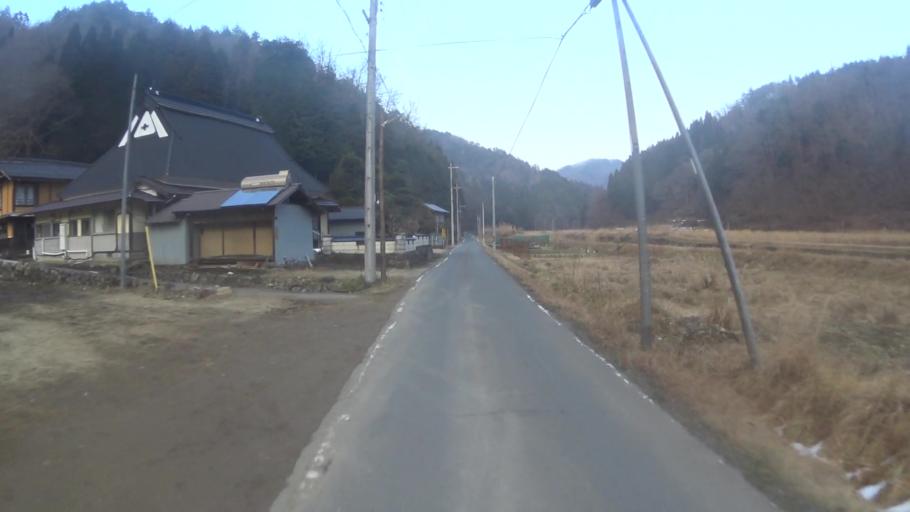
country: JP
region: Kyoto
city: Maizuru
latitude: 35.3937
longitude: 135.4722
